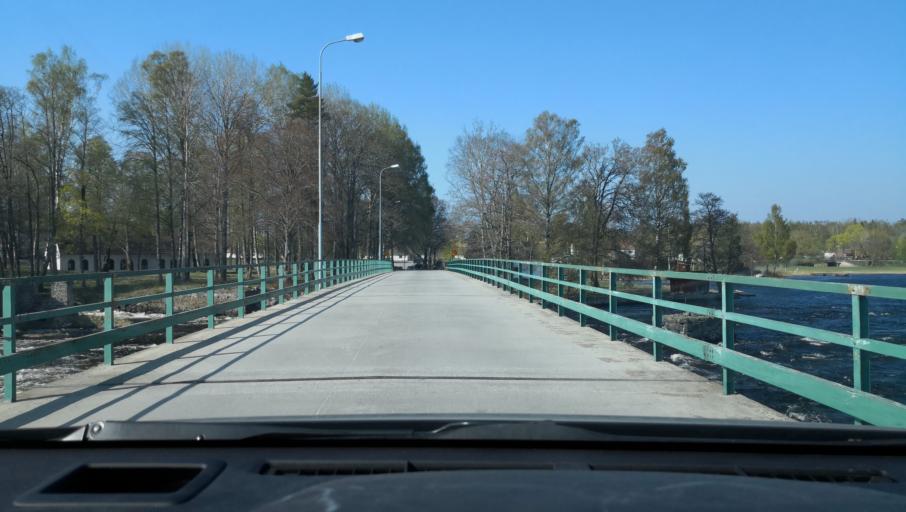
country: SE
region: Uppsala
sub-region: Heby Kommun
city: Tarnsjo
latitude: 60.2860
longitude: 16.8842
